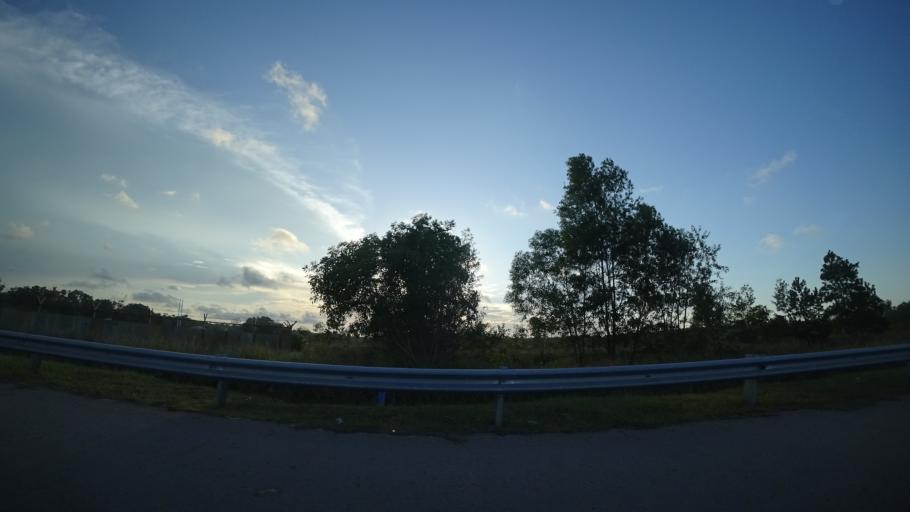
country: BN
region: Tutong
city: Tutong
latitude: 4.7924
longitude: 114.6443
